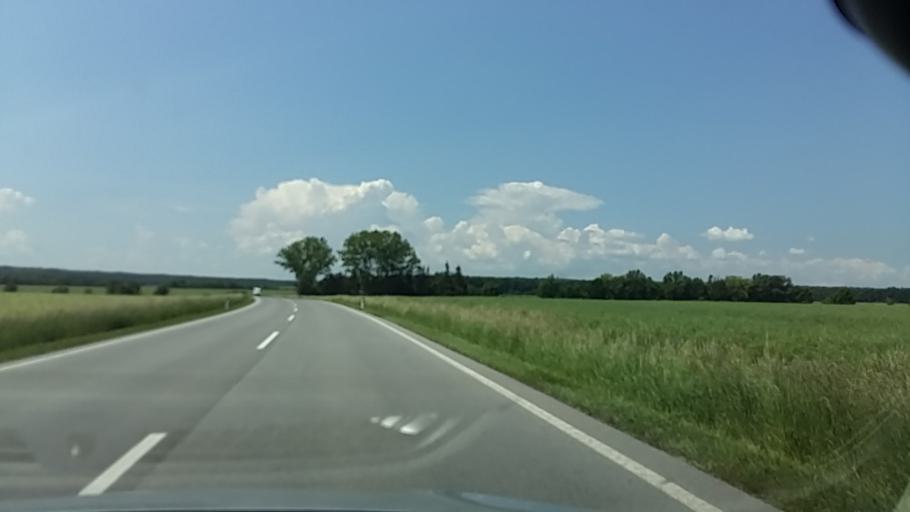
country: AT
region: Burgenland
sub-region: Politischer Bezirk Oberpullendorf
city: Raiding
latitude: 47.5353
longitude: 16.5414
